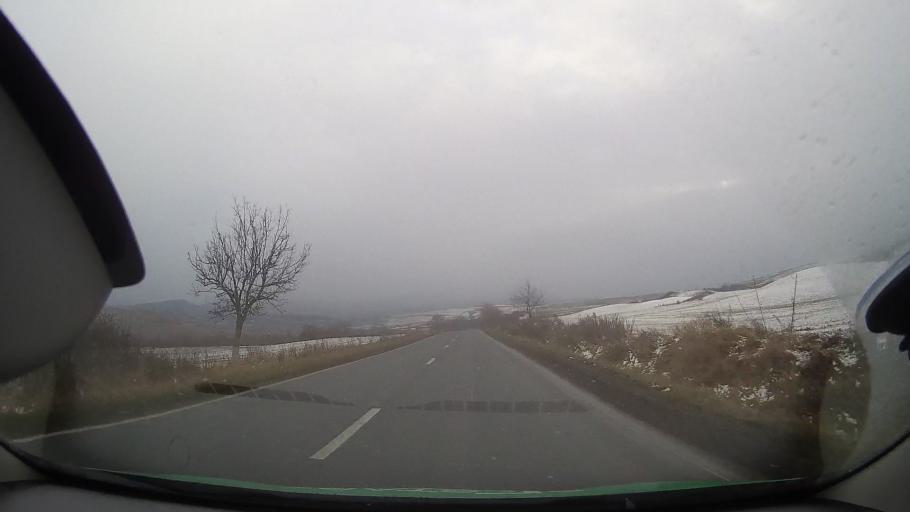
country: RO
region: Sibiu
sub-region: Comuna Blajel
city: Blajel
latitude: 46.2488
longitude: 24.3001
